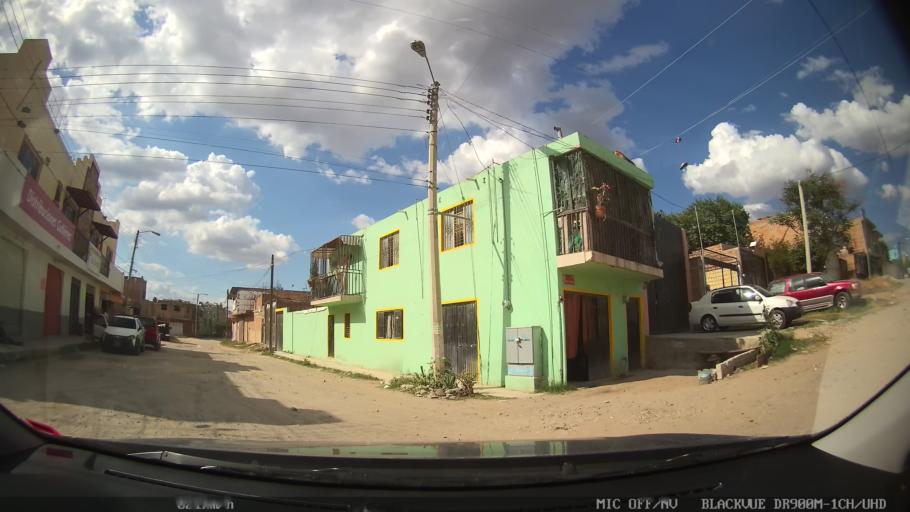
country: MX
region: Jalisco
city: Tlaquepaque
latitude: 20.6604
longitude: -103.2658
